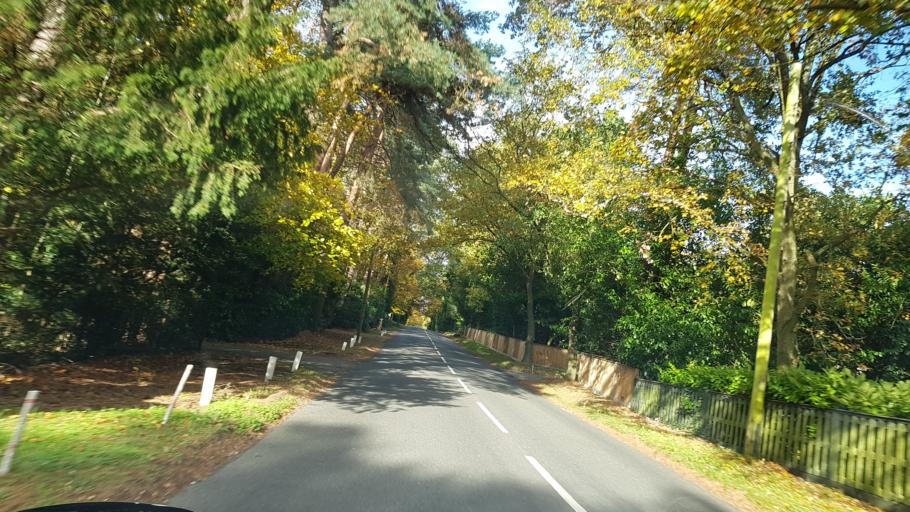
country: GB
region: England
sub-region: Surrey
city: Seale
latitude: 51.2104
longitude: -0.7501
